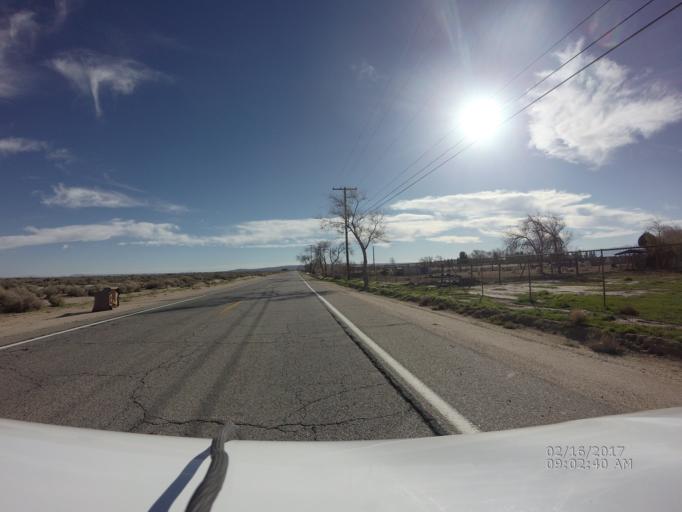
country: US
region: California
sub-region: Kern County
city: Edwards Air Force Base
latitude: 34.7637
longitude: -117.9514
